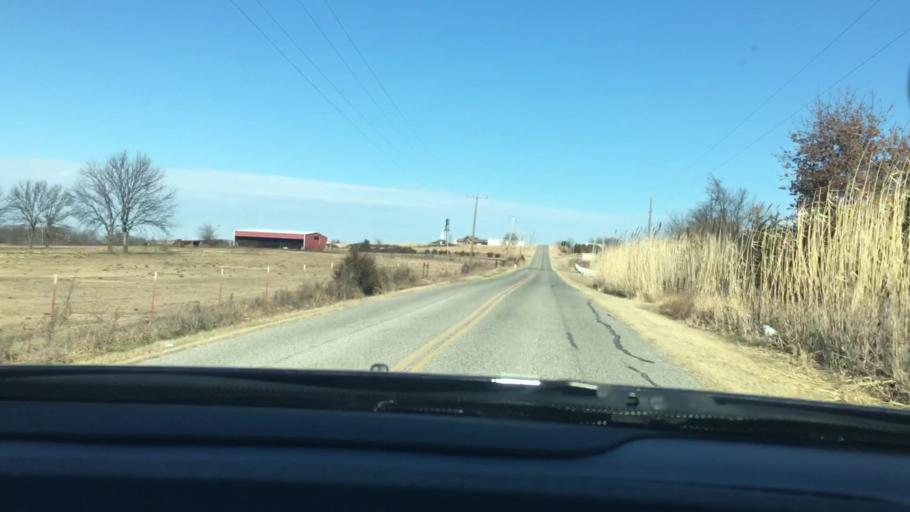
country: US
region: Oklahoma
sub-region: Murray County
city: Davis
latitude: 34.4997
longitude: -97.0553
